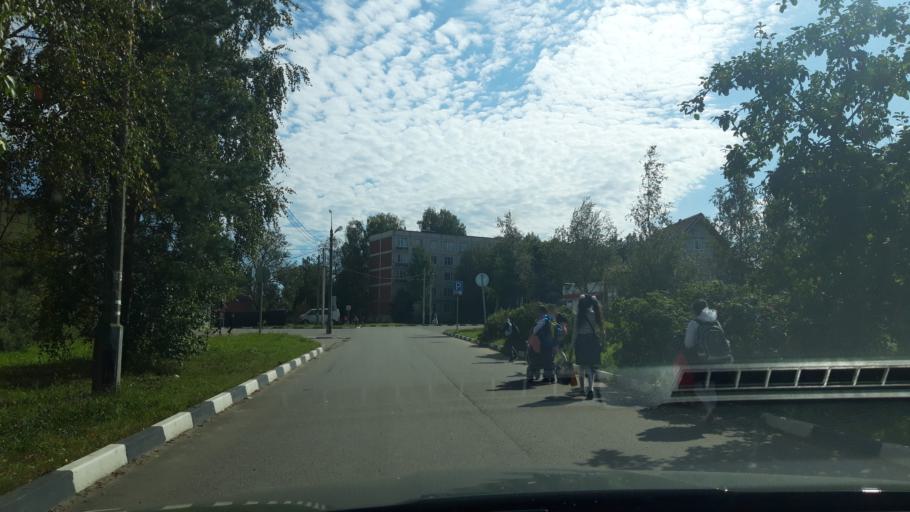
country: RU
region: Moskovskaya
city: Chashnikovo
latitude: 56.0305
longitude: 37.1719
